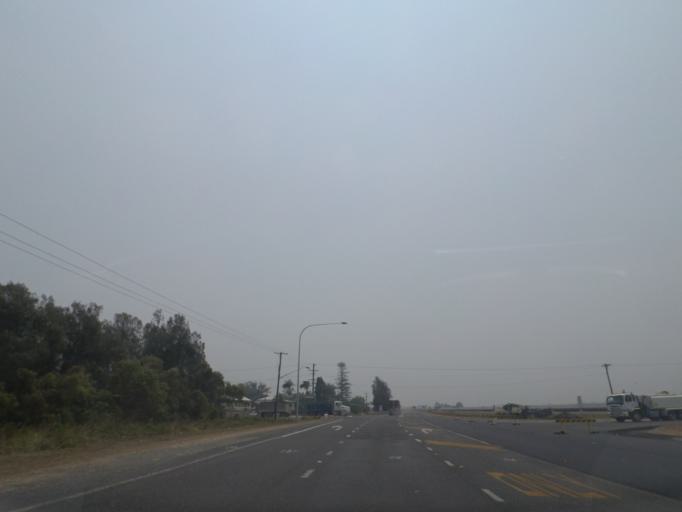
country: AU
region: New South Wales
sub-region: Clarence Valley
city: Maclean
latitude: -29.4195
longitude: 153.2407
